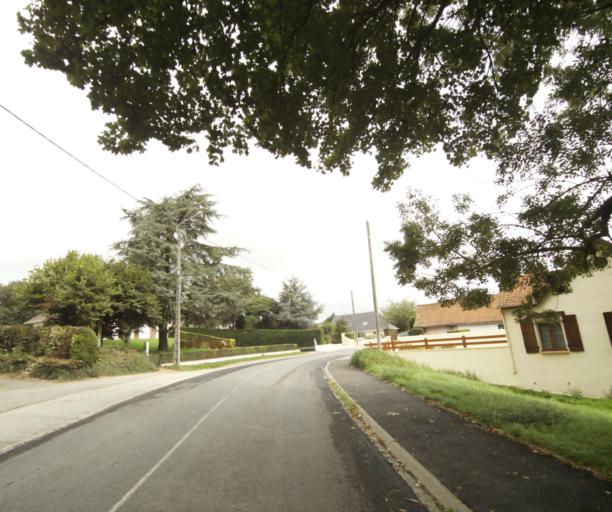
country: FR
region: Nord-Pas-de-Calais
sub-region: Departement du Pas-de-Calais
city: Etaples
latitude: 50.5251
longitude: 1.6777
